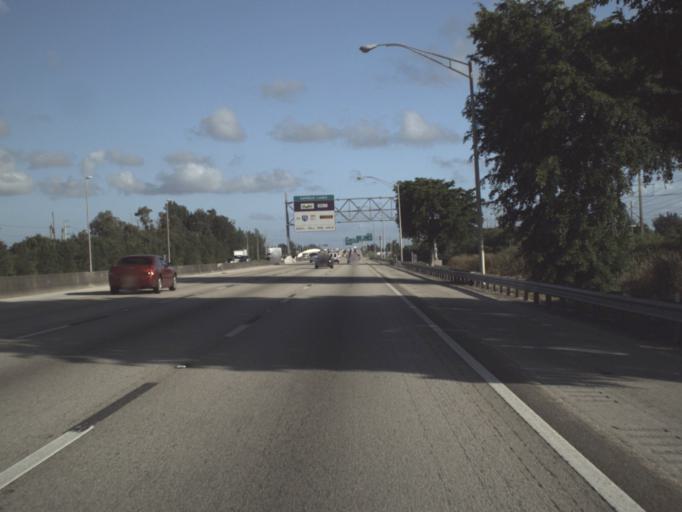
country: US
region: Florida
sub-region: Broward County
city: Davie
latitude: 26.0569
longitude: -80.2150
